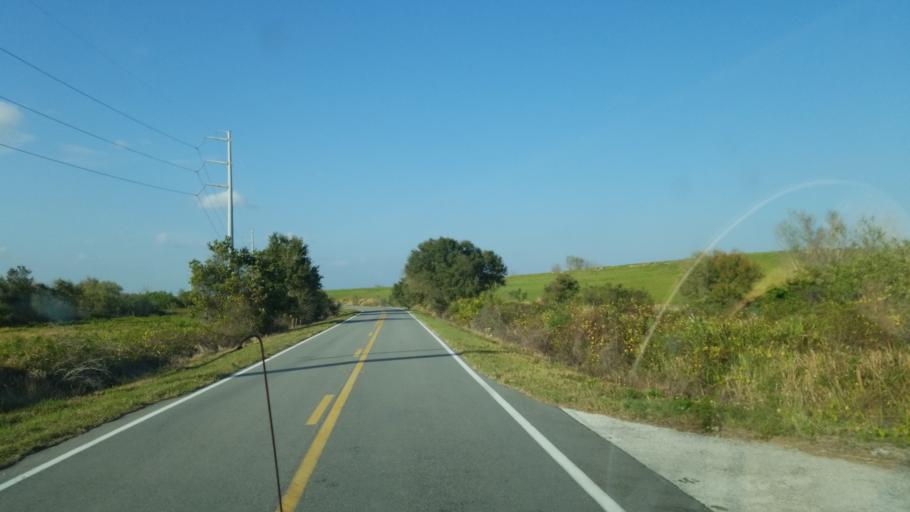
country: US
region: Florida
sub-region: Polk County
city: Mulberry
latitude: 27.7624
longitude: -81.9719
